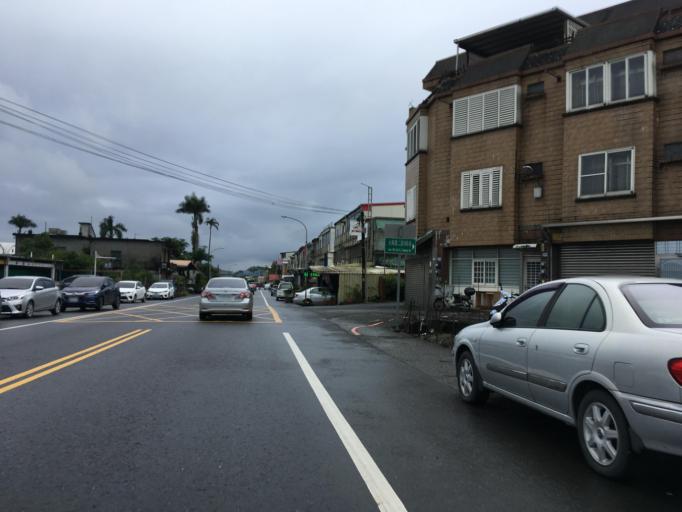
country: TW
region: Taiwan
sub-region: Yilan
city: Yilan
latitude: 24.6575
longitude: 121.7587
